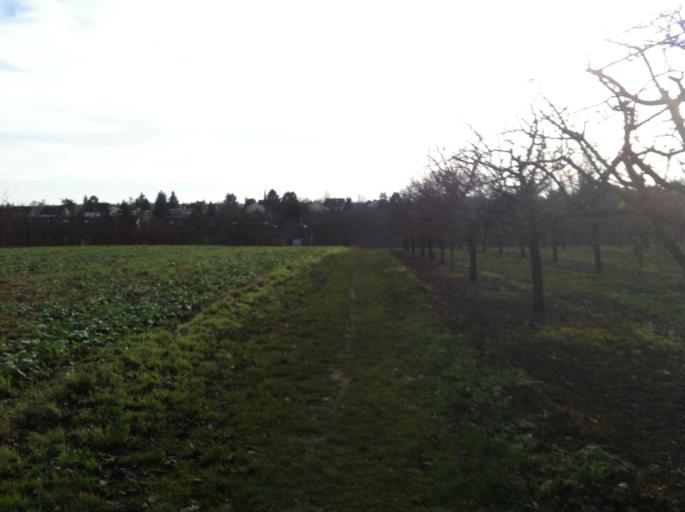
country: DE
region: Rheinland-Pfalz
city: Budenheim
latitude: 49.9942
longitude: 8.1682
